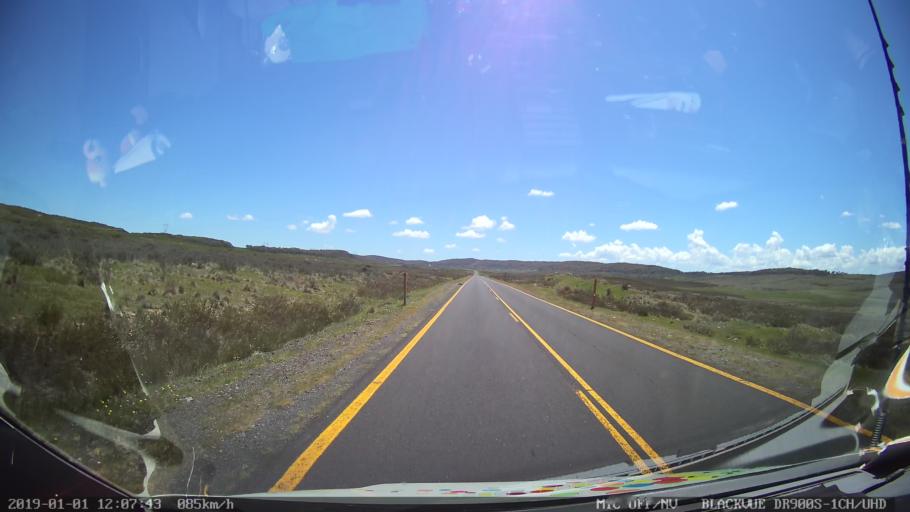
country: AU
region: New South Wales
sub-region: Tumut Shire
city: Tumut
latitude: -35.8294
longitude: 148.4911
